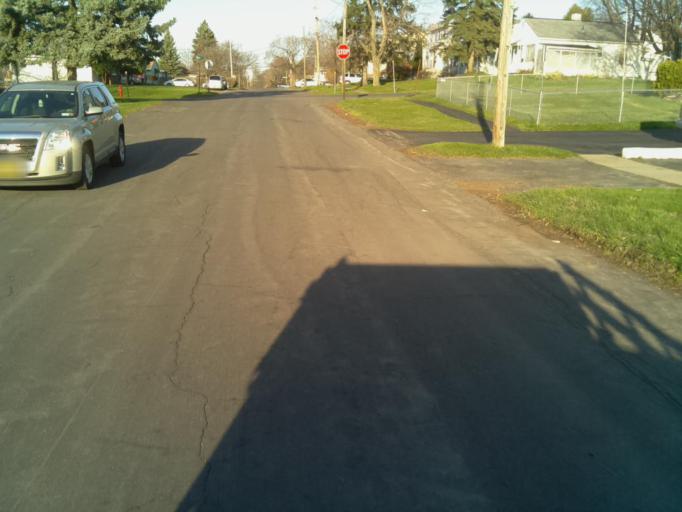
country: US
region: New York
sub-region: Onondaga County
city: East Syracuse
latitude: 43.0631
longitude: -76.0909
